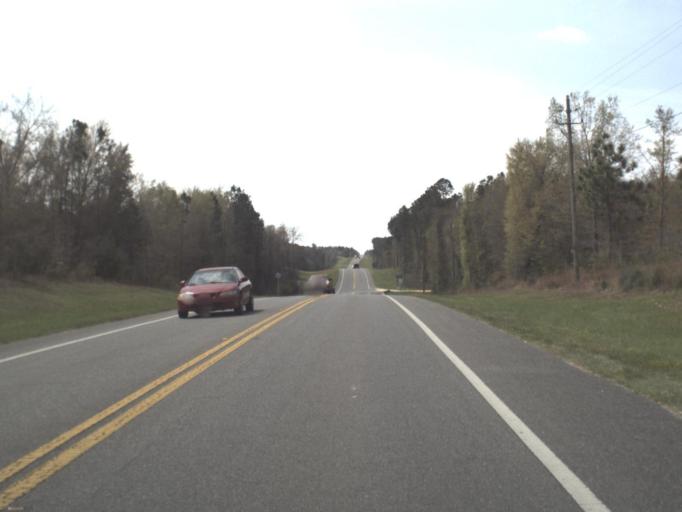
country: US
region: Florida
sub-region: Holmes County
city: Bonifay
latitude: 30.7466
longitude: -85.6851
